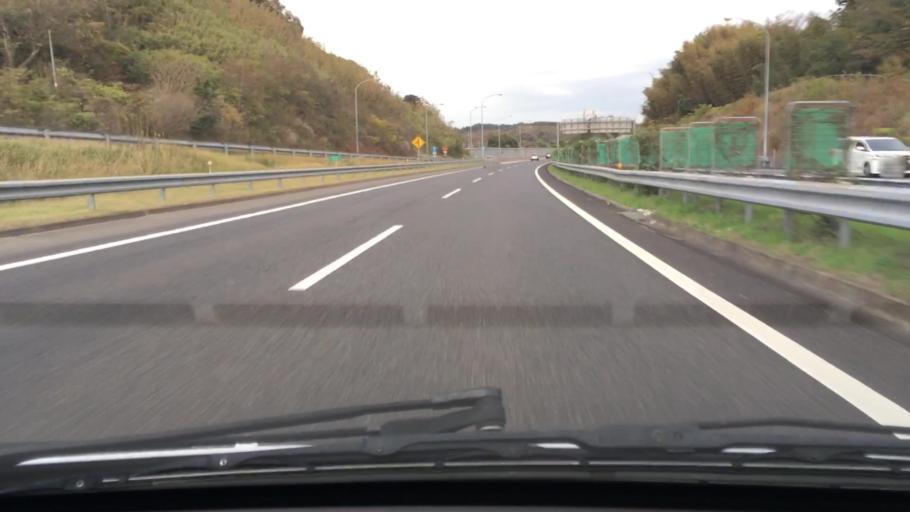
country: JP
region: Chiba
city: Kisarazu
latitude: 35.3798
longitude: 139.9841
